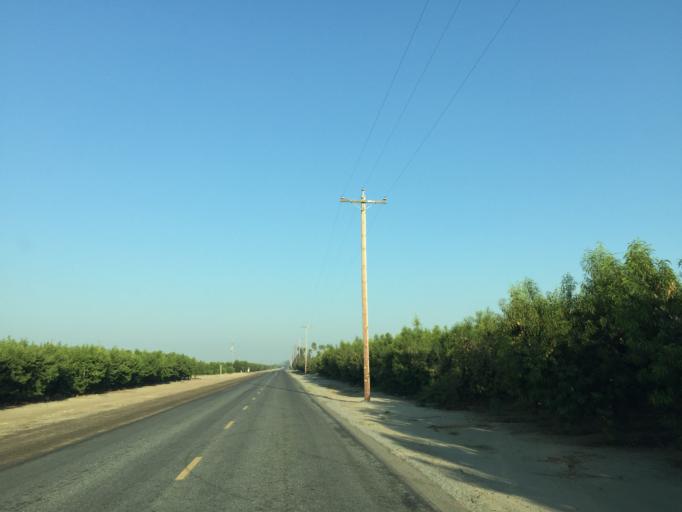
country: US
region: California
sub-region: Tulare County
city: London
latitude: 36.4588
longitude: -119.4540
